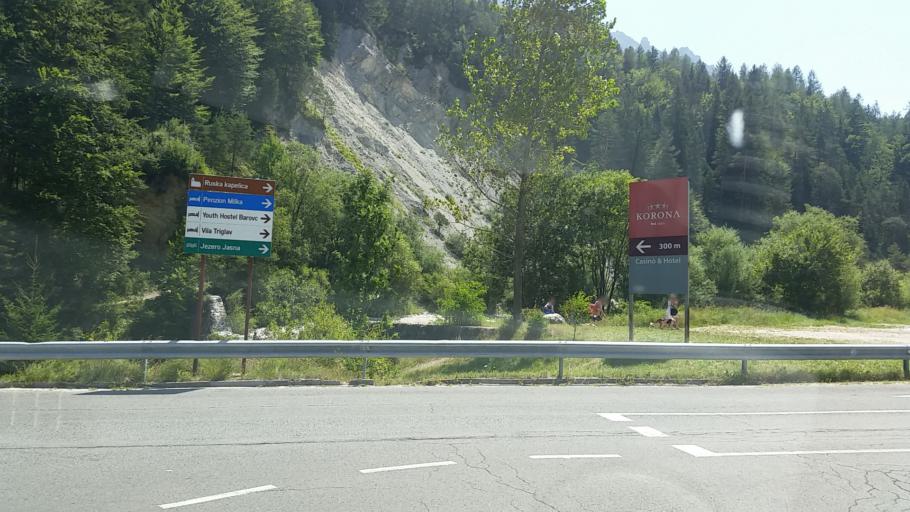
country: SI
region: Kranjska Gora
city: Kranjska Gora
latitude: 46.4817
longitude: 13.7823
